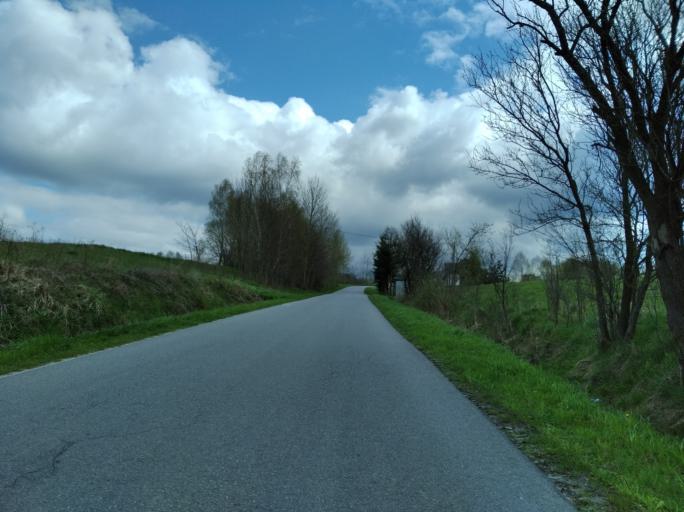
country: PL
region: Subcarpathian Voivodeship
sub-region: Powiat strzyzowski
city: Polomia
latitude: 49.8842
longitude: 21.9072
